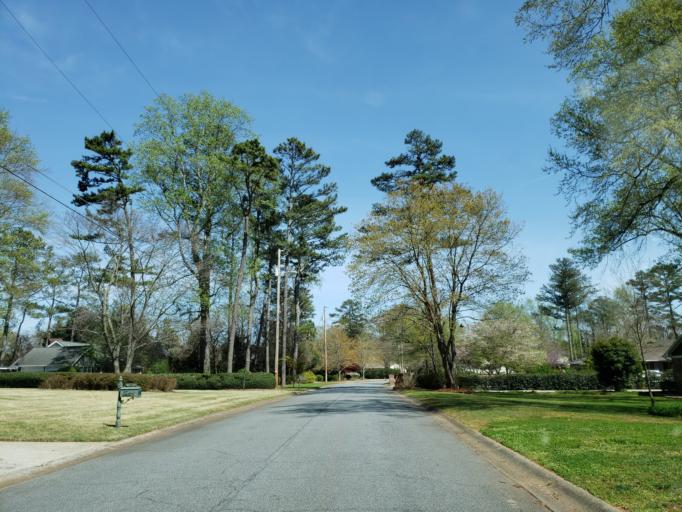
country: US
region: Georgia
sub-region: Cobb County
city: Marietta
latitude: 33.9624
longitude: -84.5623
